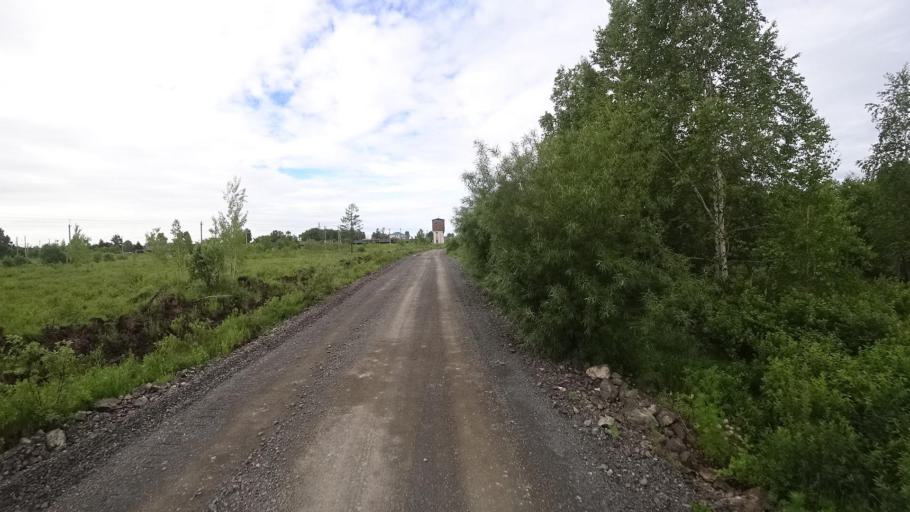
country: RU
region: Khabarovsk Krai
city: Amursk
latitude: 49.9023
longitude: 136.1373
